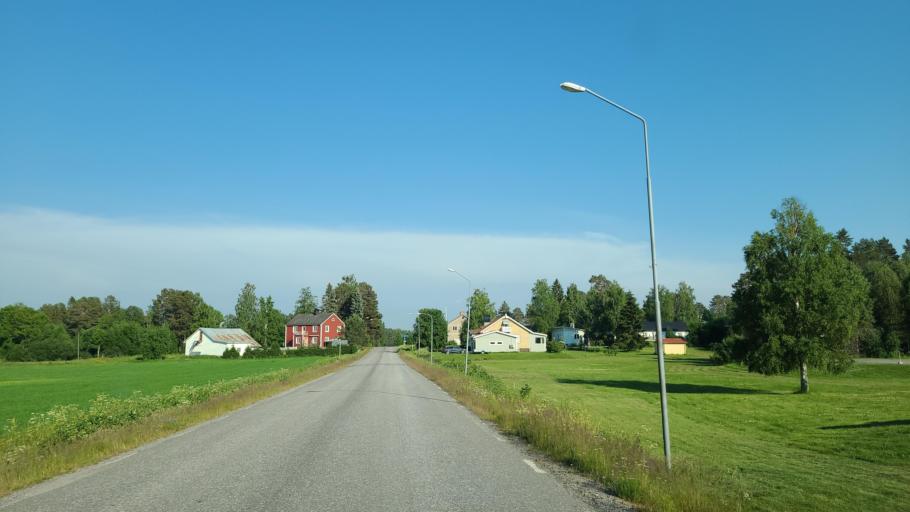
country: SE
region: Vaesterbotten
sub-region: Robertsfors Kommun
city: Robertsfors
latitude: 64.3036
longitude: 20.8639
